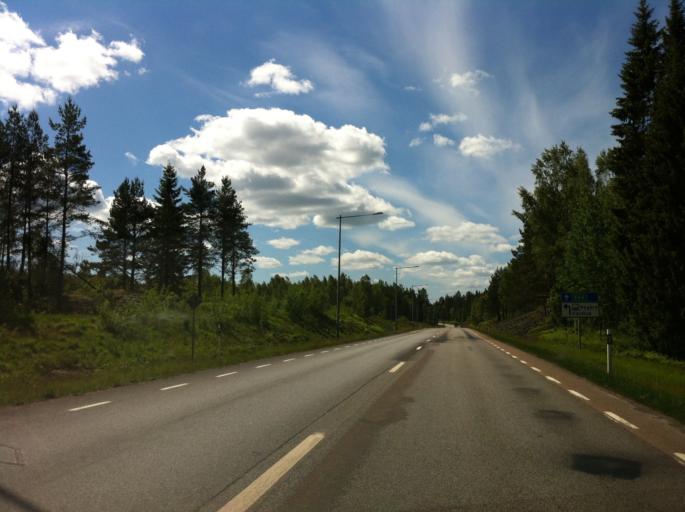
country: SE
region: Vaestra Goetaland
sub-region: Amals Kommun
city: Amal
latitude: 59.0420
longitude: 12.6765
